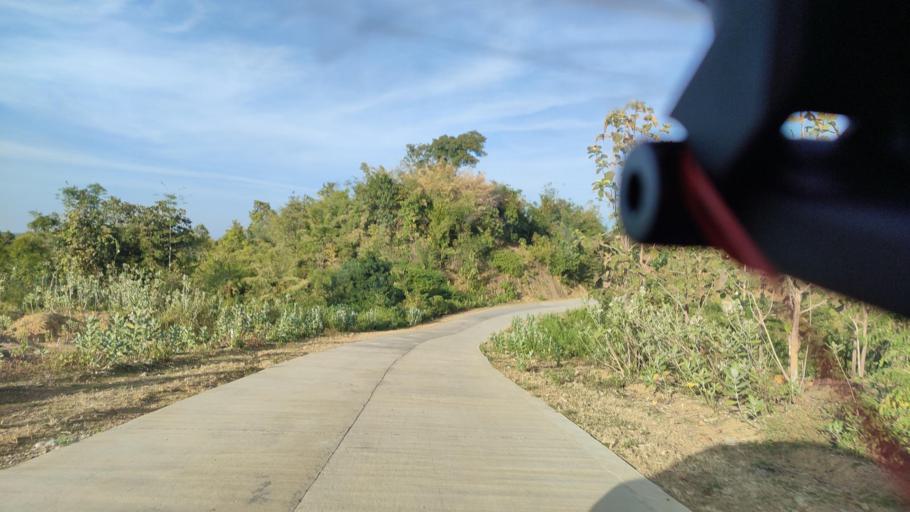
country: MM
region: Magway
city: Taungdwingyi
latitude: 20.0203
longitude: 95.8164
